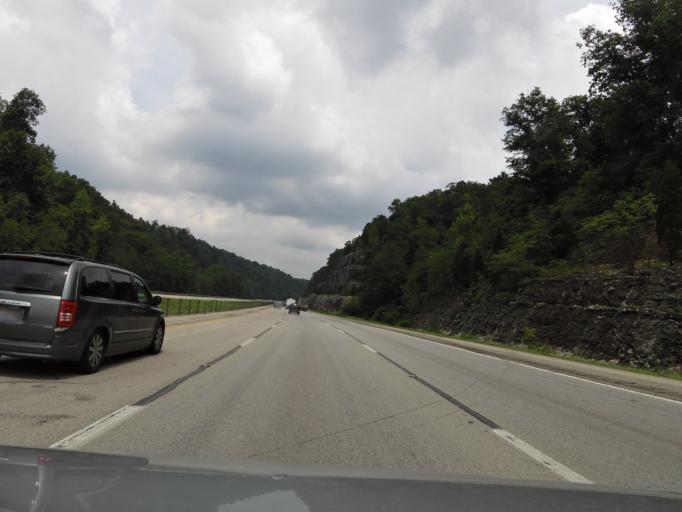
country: US
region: Kentucky
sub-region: Hardin County
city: Elizabethtown
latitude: 37.7473
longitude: -85.7939
